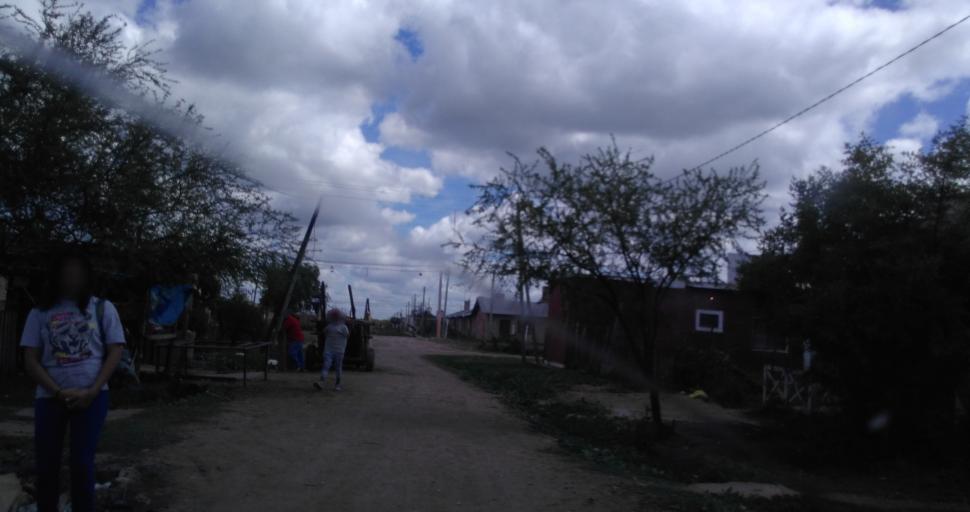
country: AR
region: Chaco
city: Resistencia
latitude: -27.4820
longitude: -59.0085
